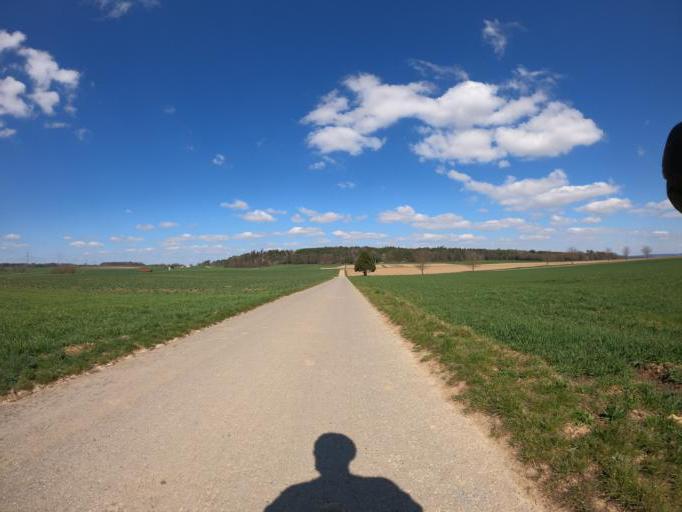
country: DE
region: Baden-Wuerttemberg
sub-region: Regierungsbezirk Stuttgart
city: Bondorf
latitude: 48.4774
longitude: 8.8643
